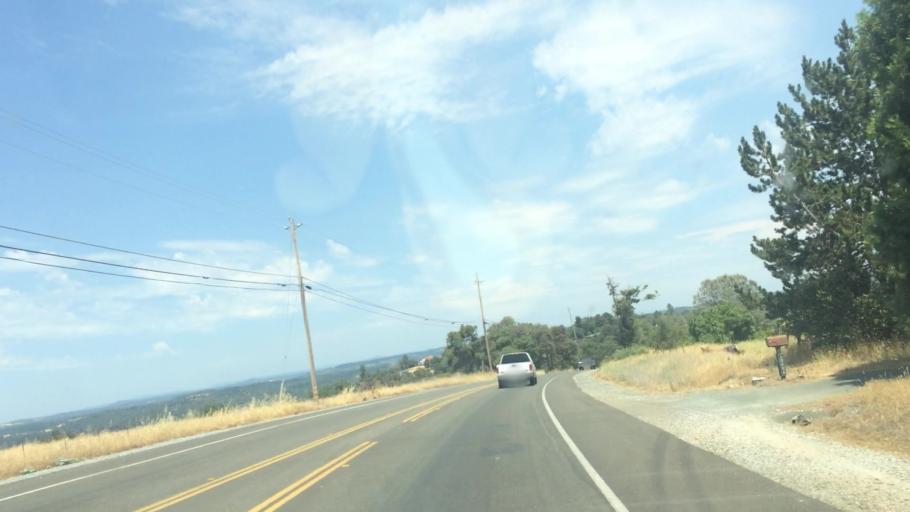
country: US
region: California
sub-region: Amador County
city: Sutter Creek
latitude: 38.3852
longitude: -120.7853
